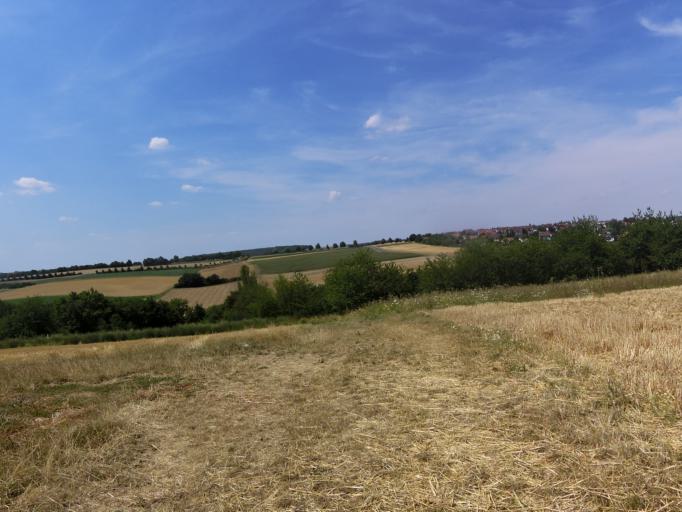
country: DE
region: Bavaria
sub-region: Regierungsbezirk Unterfranken
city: Estenfeld
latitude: 49.8179
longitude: 10.0033
